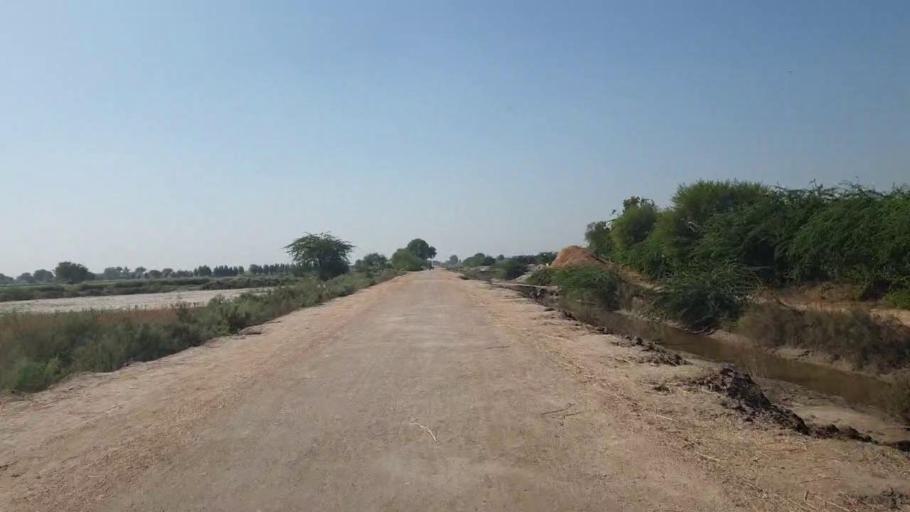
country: PK
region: Sindh
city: Talhar
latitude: 24.8214
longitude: 68.7643
